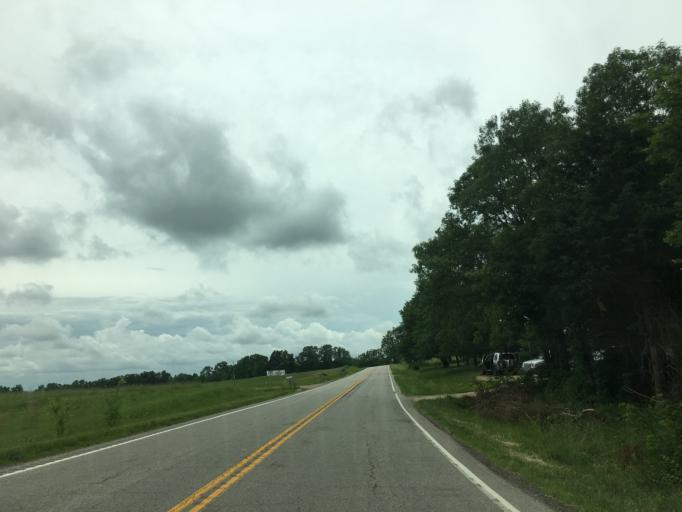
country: US
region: Missouri
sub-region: Gasconade County
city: Owensville
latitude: 38.4758
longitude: -91.4626
